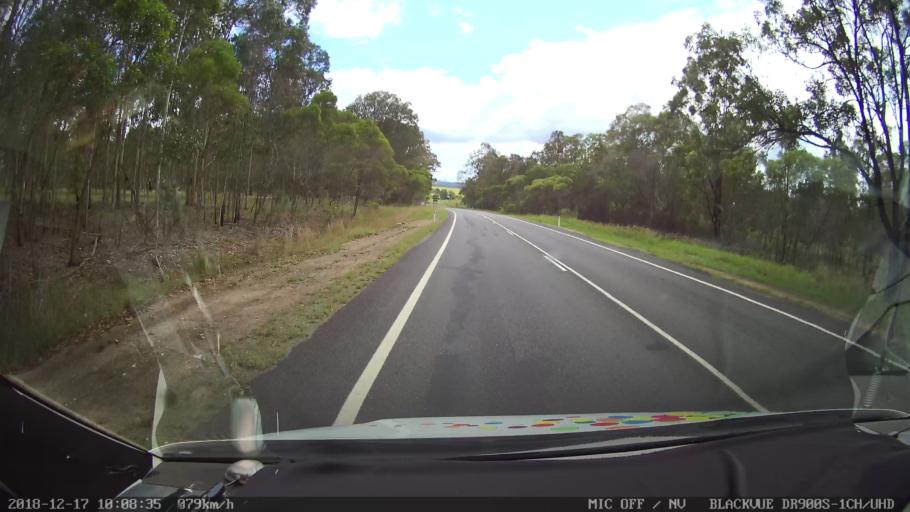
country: AU
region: New South Wales
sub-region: Tenterfield Municipality
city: Carrolls Creek
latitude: -28.8907
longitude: 152.5335
